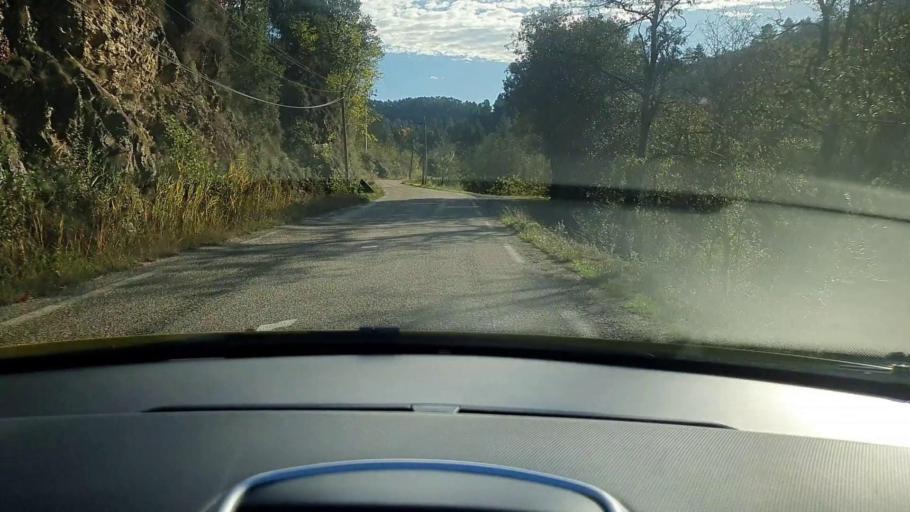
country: FR
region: Languedoc-Roussillon
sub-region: Departement du Gard
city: Valleraugue
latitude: 44.1270
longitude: 3.7528
